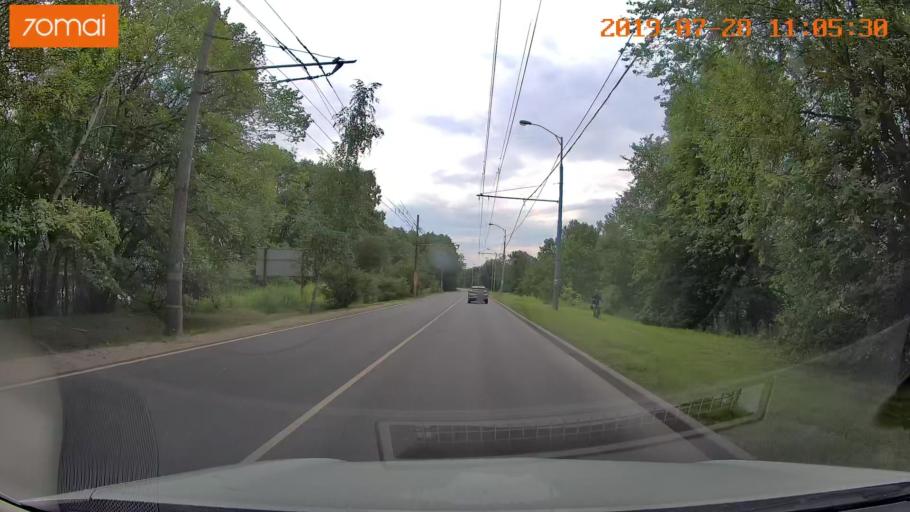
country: RU
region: Kaliningrad
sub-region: Gorod Kaliningrad
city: Kaliningrad
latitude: 54.7178
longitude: 20.3937
